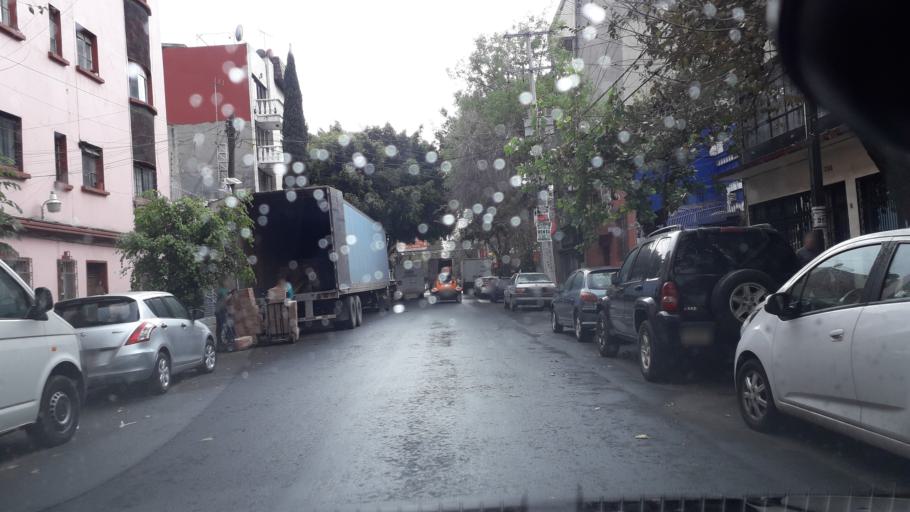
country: MX
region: Mexico City
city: Cuauhtemoc
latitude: 19.4530
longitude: -99.1555
